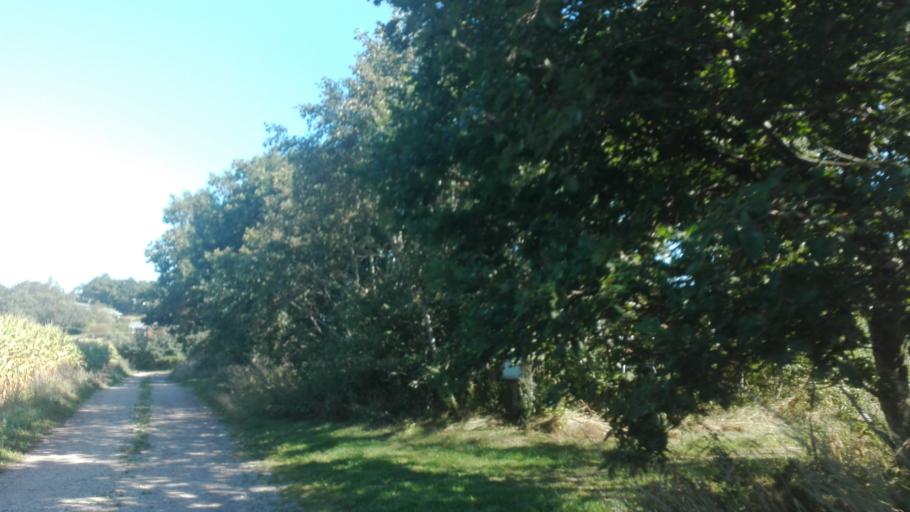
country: DK
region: Central Jutland
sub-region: Syddjurs Kommune
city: Ebeltoft
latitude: 56.2292
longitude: 10.7441
